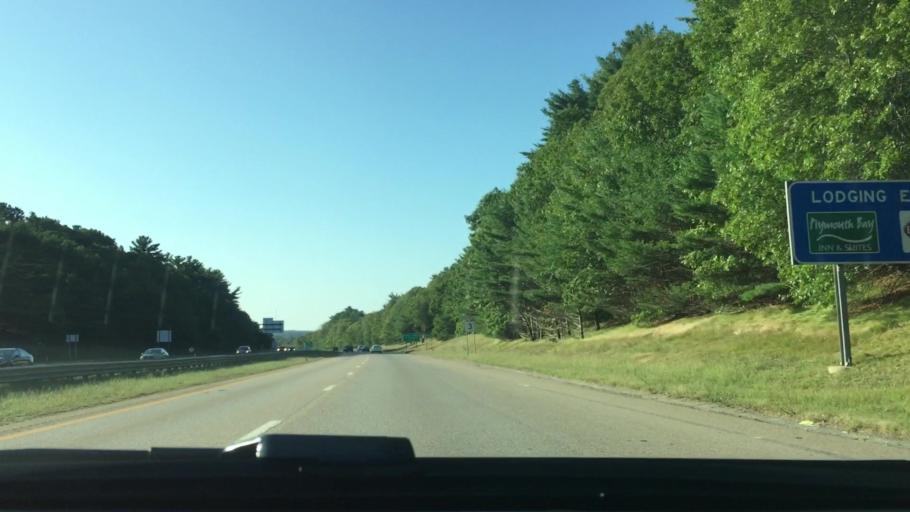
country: US
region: Massachusetts
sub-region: Plymouth County
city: Kingston
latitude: 42.0129
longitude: -70.7266
